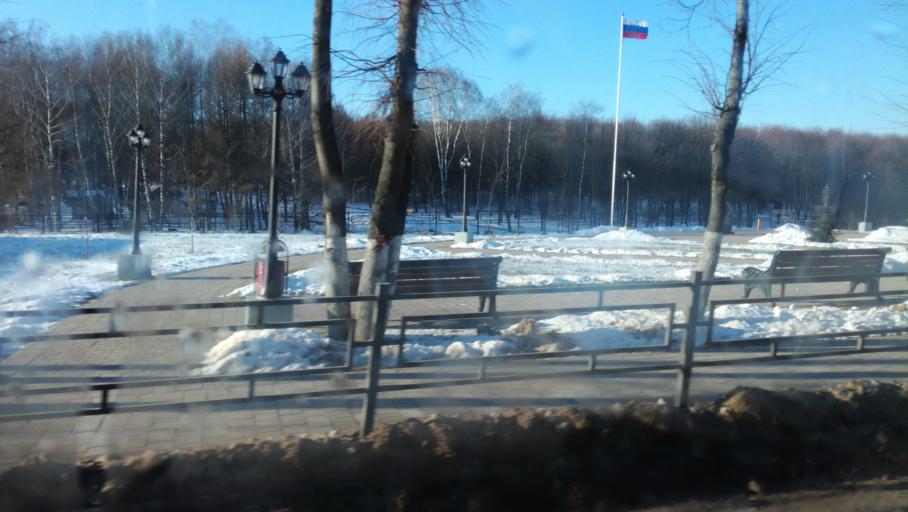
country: RU
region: Tula
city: Kosaya Gora
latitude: 54.1927
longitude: 37.5358
